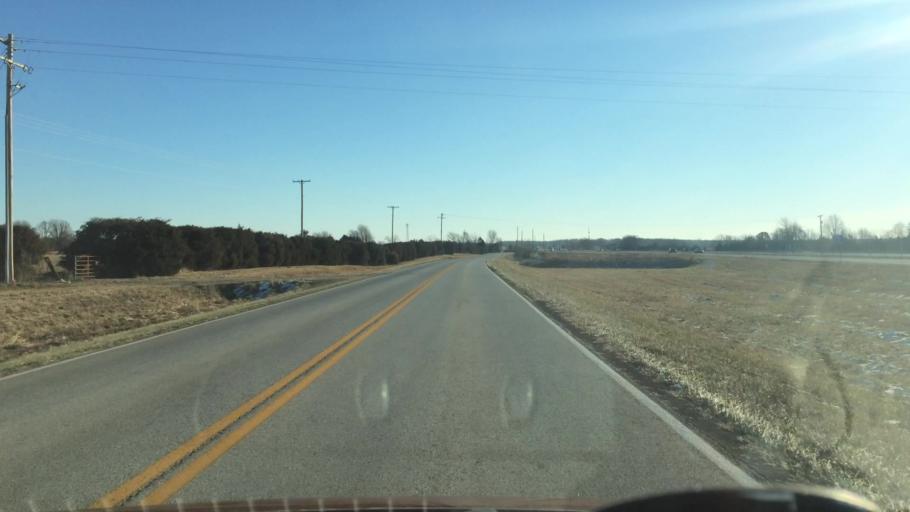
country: US
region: Missouri
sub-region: Greene County
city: Strafford
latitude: 37.2717
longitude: -93.1048
